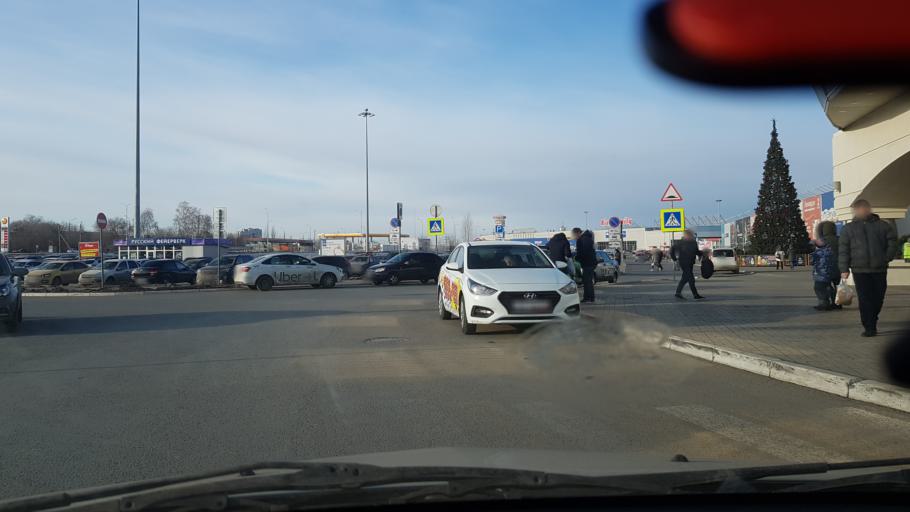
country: RU
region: Samara
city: Tol'yatti
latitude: 53.5412
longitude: 49.3894
